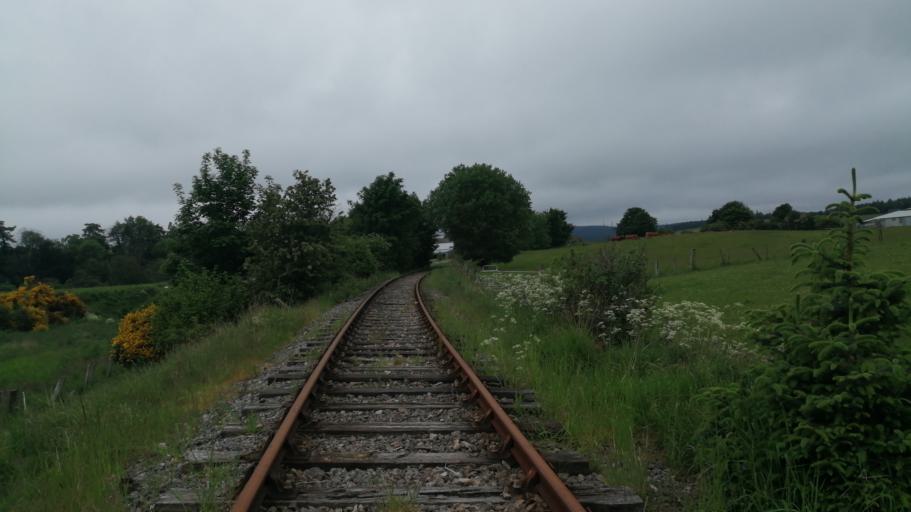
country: GB
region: Scotland
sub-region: Moray
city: Keith
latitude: 57.5343
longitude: -2.9638
